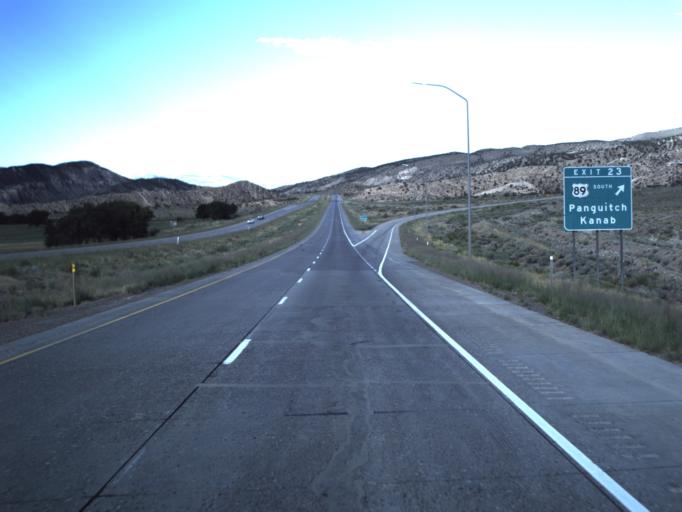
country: US
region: Utah
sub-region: Sevier County
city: Monroe
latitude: 38.6032
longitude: -112.2414
